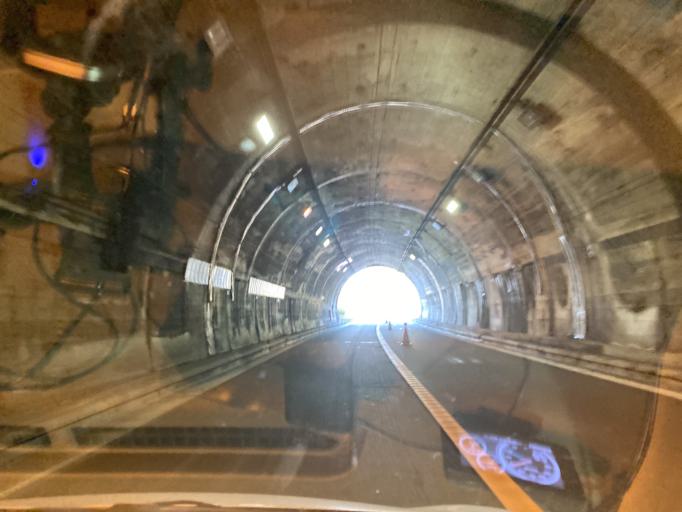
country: JP
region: Wakayama
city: Iwade
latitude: 34.3052
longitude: 135.2703
